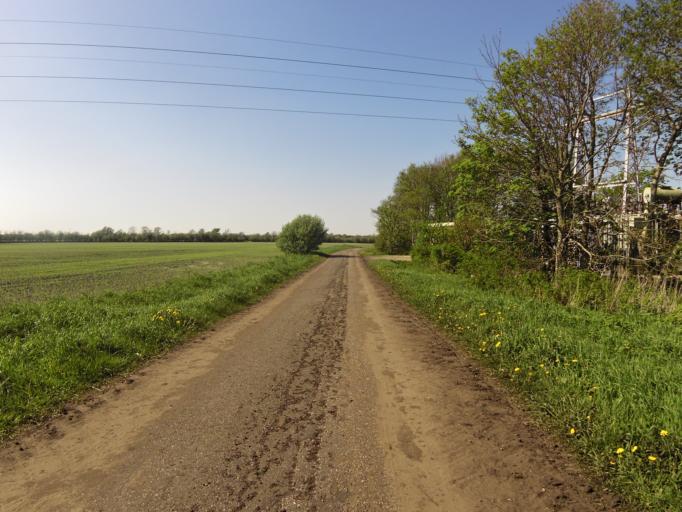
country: DK
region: South Denmark
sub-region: Tonder Kommune
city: Sherrebek
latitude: 55.2084
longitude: 8.8442
